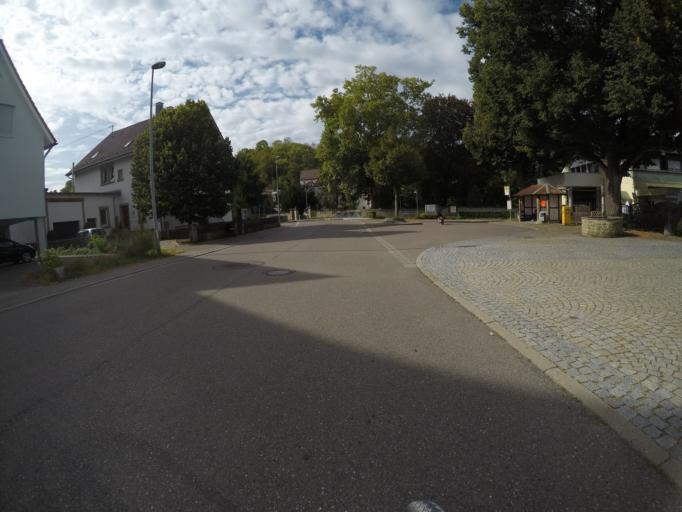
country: DE
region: Baden-Wuerttemberg
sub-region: Regierungsbezirk Stuttgart
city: Eberdingen
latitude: 48.8953
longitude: 8.9722
